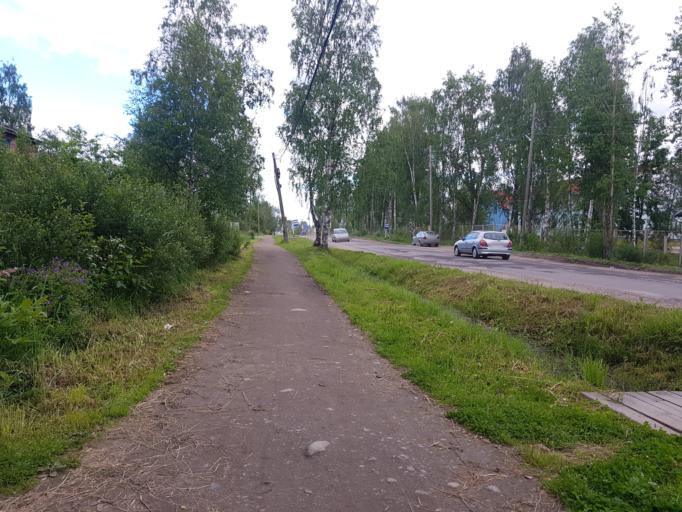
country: RU
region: Republic of Karelia
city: Kalevala
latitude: 65.2030
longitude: 31.1743
